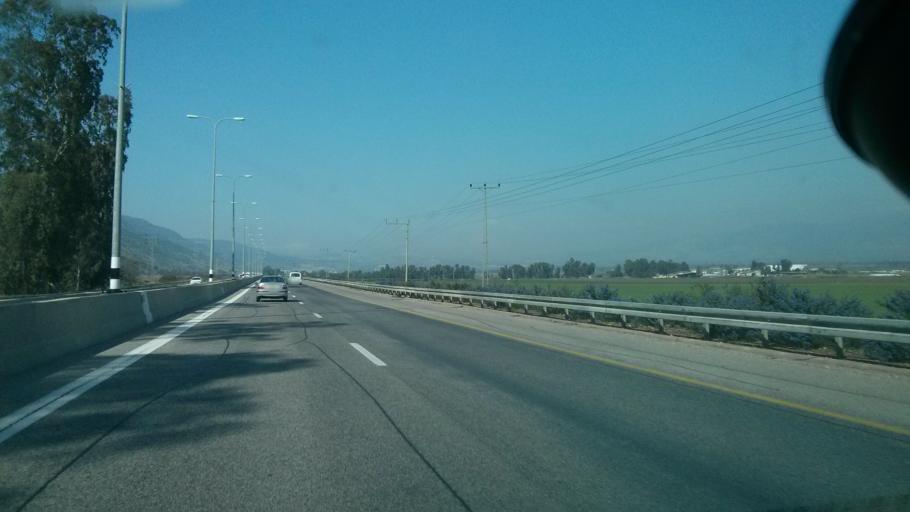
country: IL
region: Northern District
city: Qiryat Shemona
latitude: 33.0989
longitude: 35.5745
